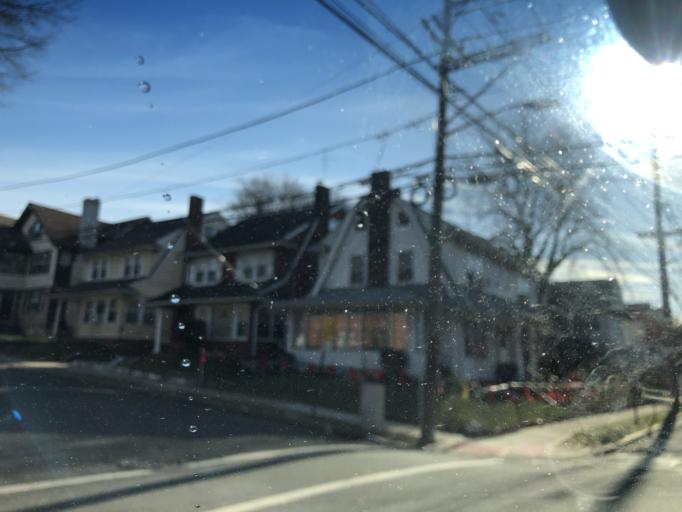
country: US
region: New Jersey
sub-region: Bergen County
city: Fair Lawn
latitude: 40.9160
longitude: -74.1422
